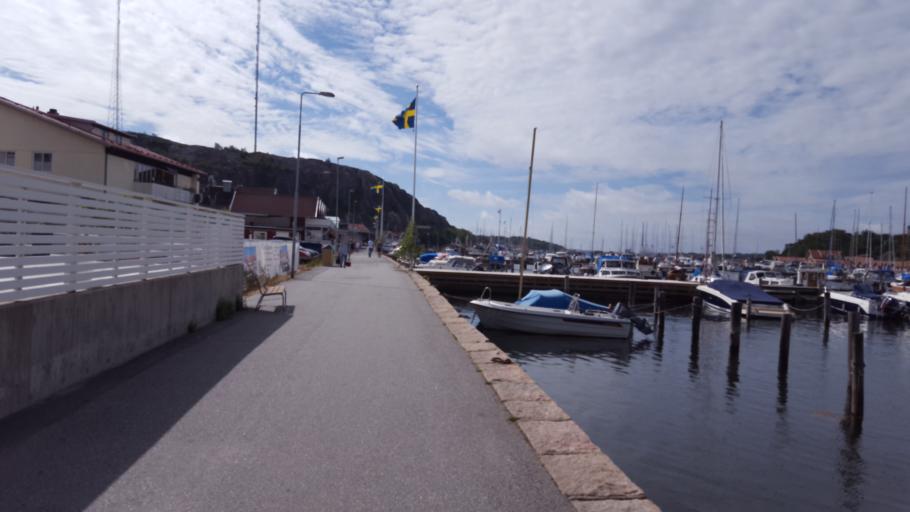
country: SE
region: Vaestra Goetaland
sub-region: Tanums Kommun
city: Grebbestad
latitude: 58.6913
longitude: 11.2546
